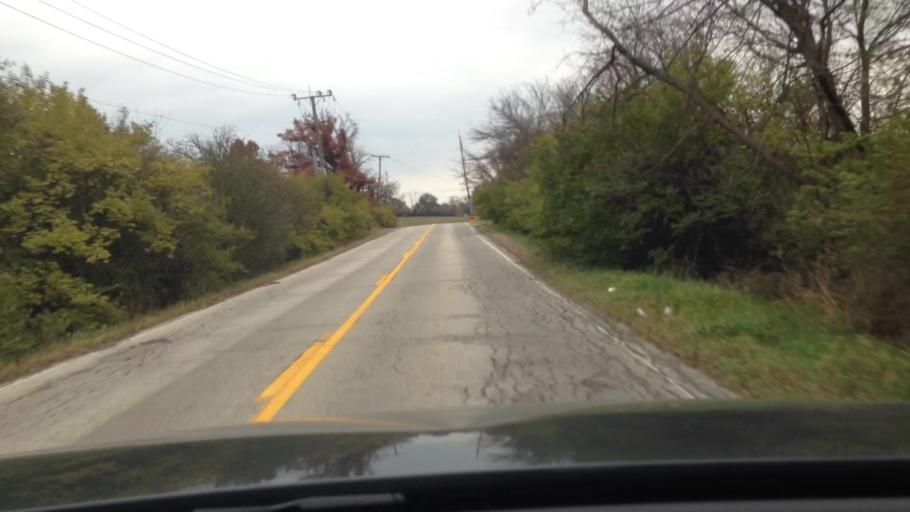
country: US
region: Illinois
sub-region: McHenry County
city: Woodstock
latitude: 42.2712
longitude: -88.4352
